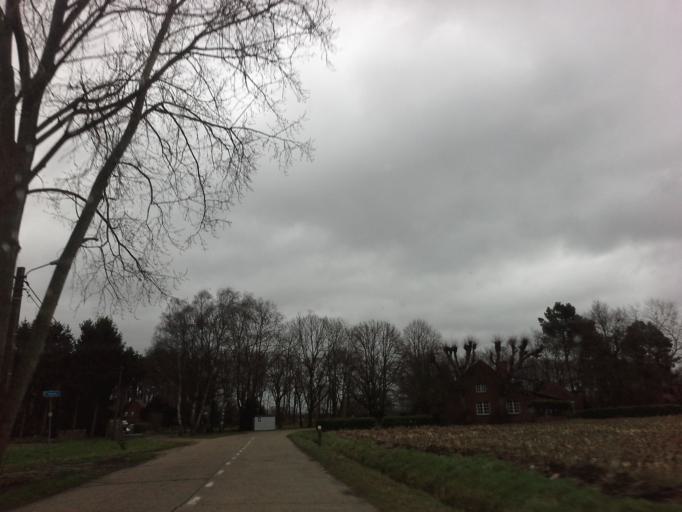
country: BE
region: Flanders
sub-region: Provincie Antwerpen
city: Meerhout
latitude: 51.1311
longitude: 5.0525
